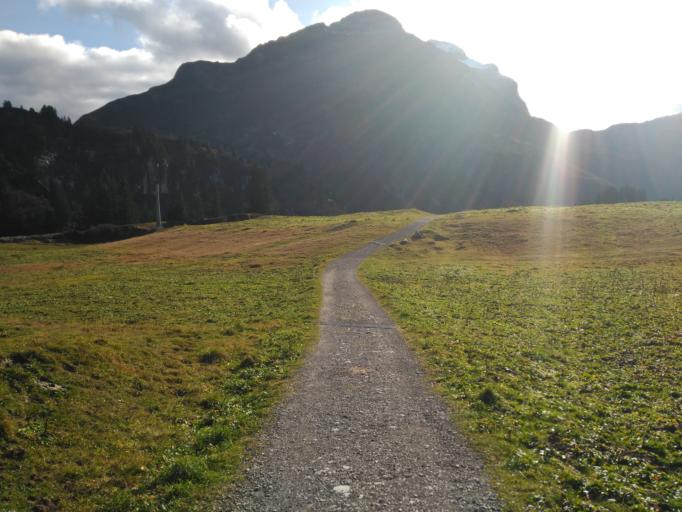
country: AT
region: Vorarlberg
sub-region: Politischer Bezirk Bregenz
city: Schroecken
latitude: 47.2567
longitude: 10.1102
